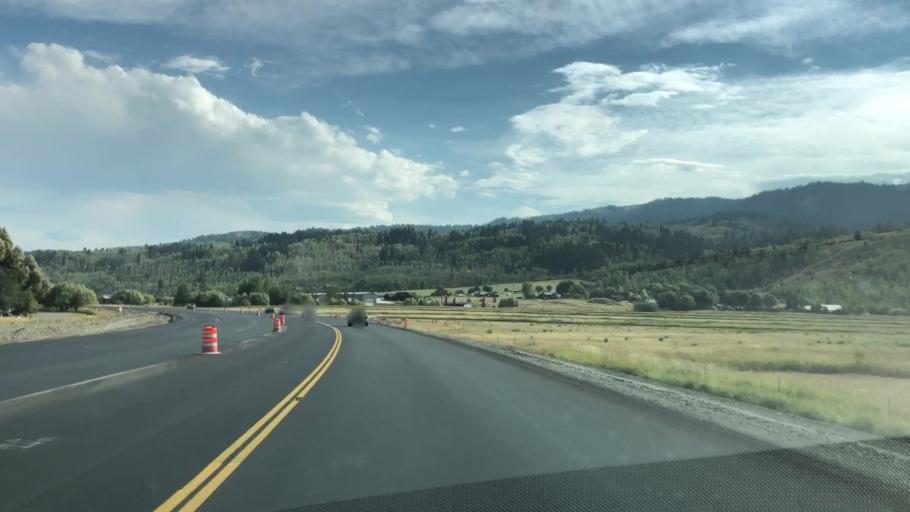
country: US
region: Wyoming
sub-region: Teton County
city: South Park
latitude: 43.3772
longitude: -110.7450
